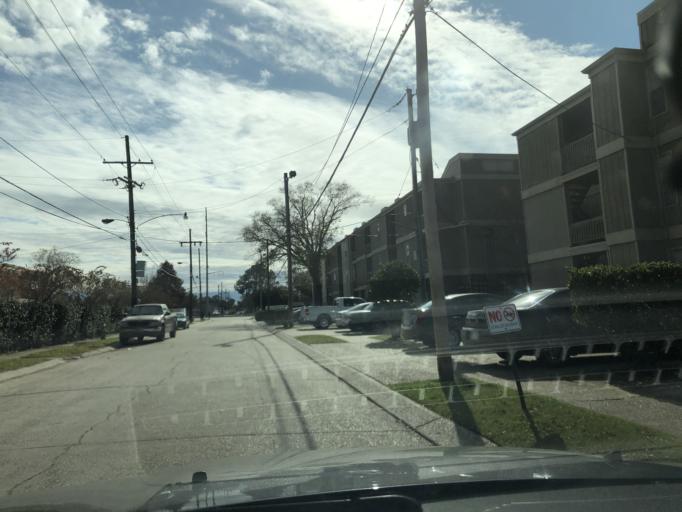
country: US
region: Louisiana
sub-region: Jefferson Parish
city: Metairie
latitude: 29.9939
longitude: -90.1610
